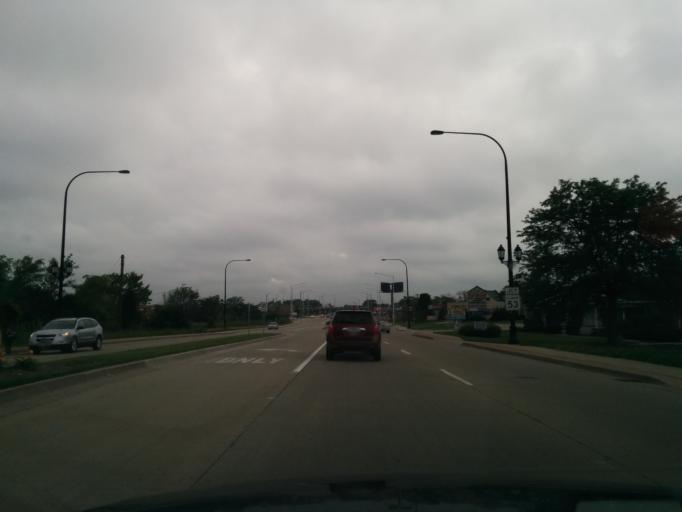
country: US
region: Illinois
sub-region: DuPage County
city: Itasca
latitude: 41.9490
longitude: -88.0283
